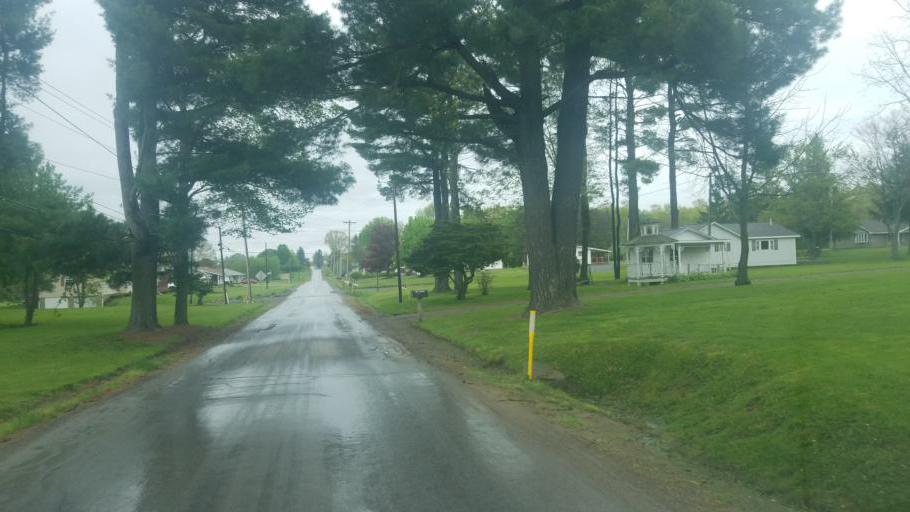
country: US
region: Pennsylvania
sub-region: Forest County
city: Tionesta
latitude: 41.3957
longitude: -79.3881
